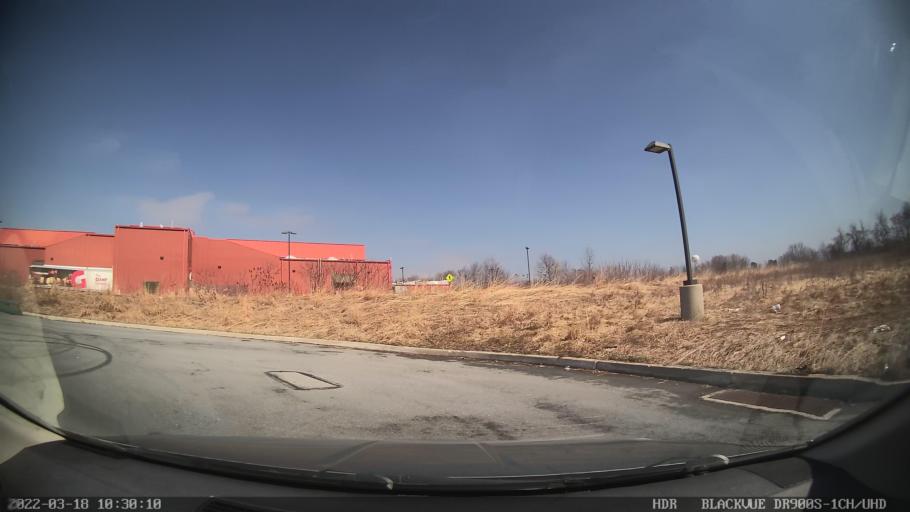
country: US
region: Pennsylvania
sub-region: Berks County
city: Kutztown
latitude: 40.5023
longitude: -75.7881
